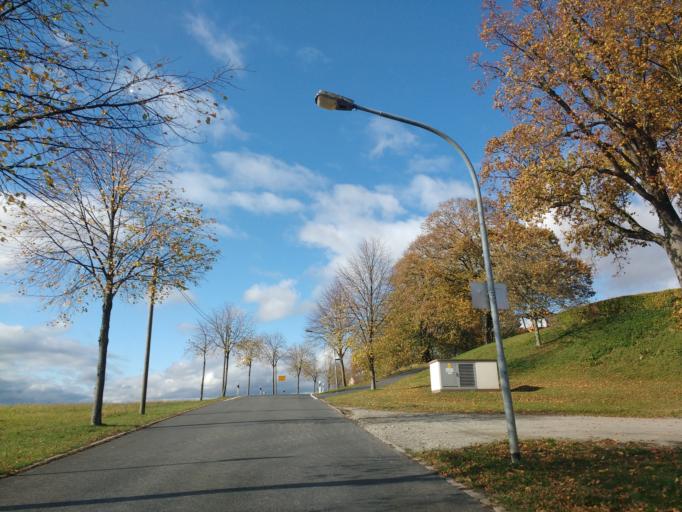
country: DE
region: Thuringia
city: Worbis
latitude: 51.4446
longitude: 10.3555
